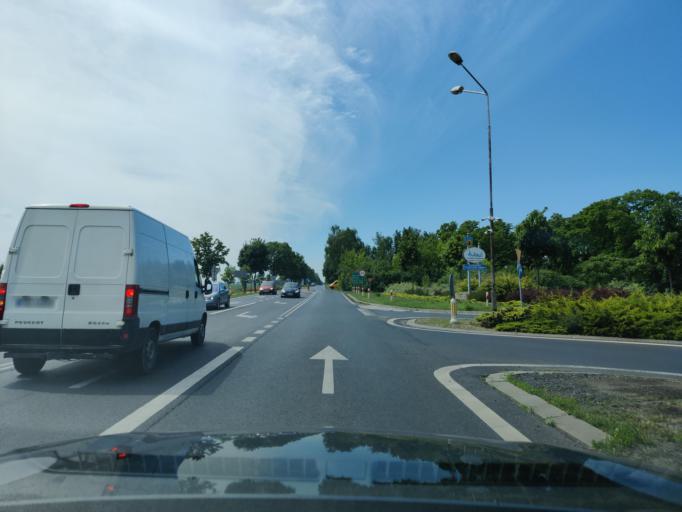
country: PL
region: Greater Poland Voivodeship
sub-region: Powiat grodziski
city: Grodzisk Wielkopolski
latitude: 52.2149
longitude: 16.3643
